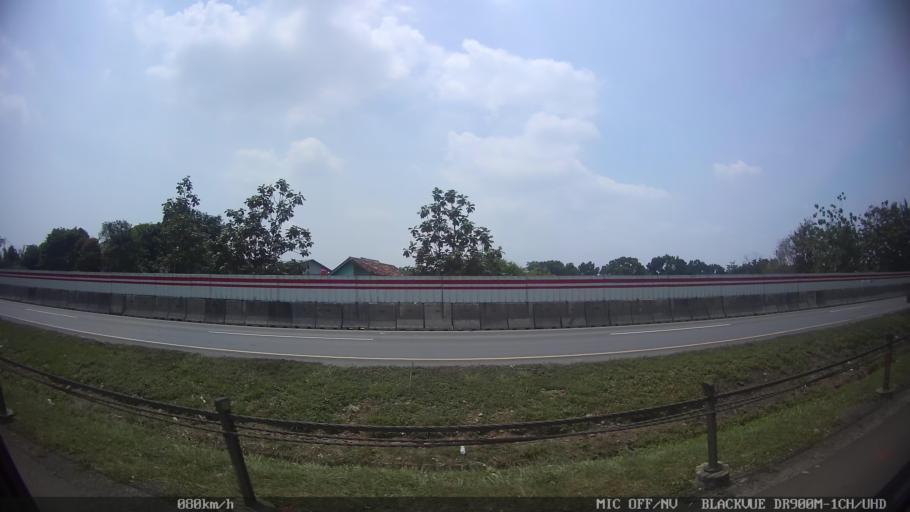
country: ID
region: West Java
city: Kresek
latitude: -6.1439
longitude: 106.2896
